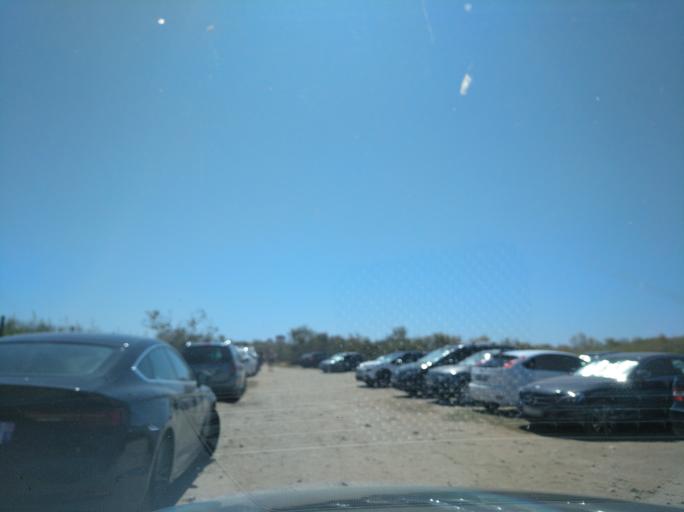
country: PT
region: Faro
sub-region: Vila Real de Santo Antonio
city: Monte Gordo
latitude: 37.1745
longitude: -7.4931
